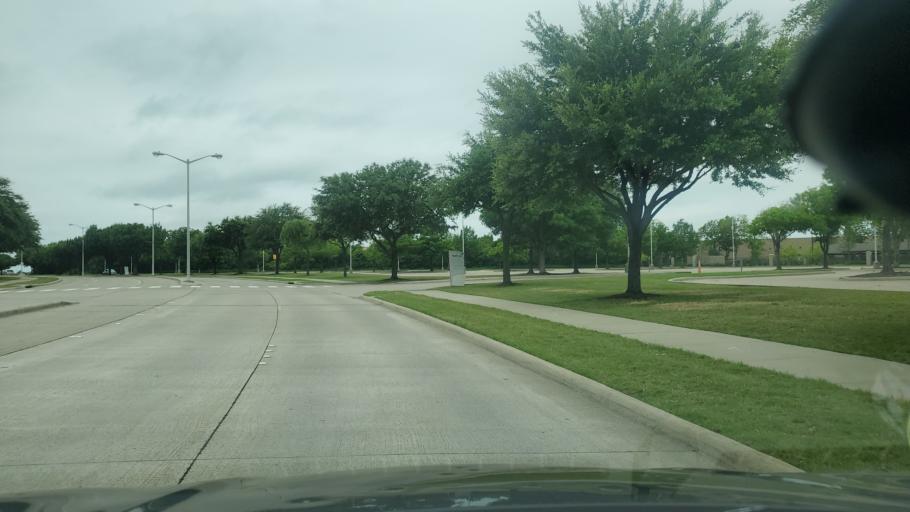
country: US
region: Texas
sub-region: Dallas County
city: Sachse
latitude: 32.9606
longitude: -96.6405
